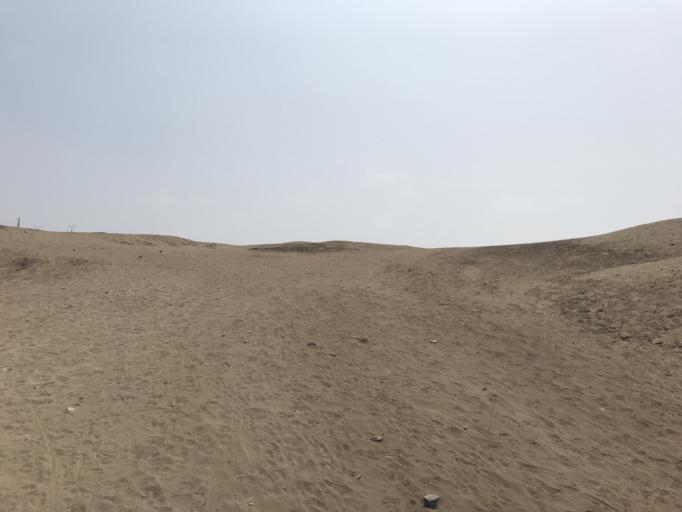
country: PE
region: Lima
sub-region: Lima
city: Punta Hermosa
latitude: -12.2562
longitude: -76.9068
